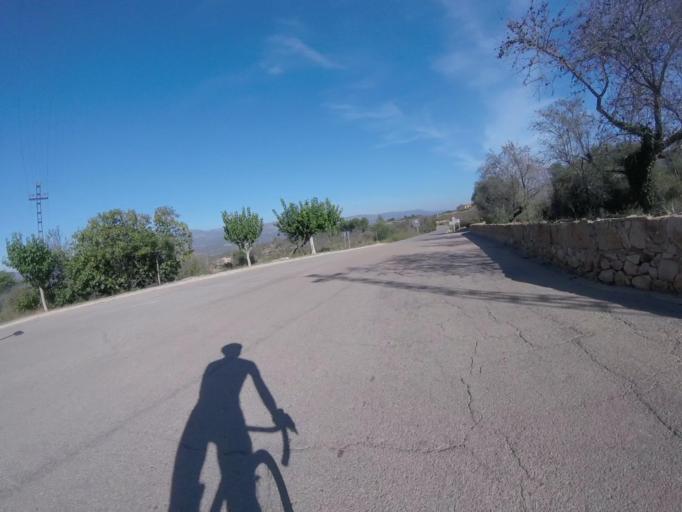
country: ES
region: Valencia
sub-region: Provincia de Castello
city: Benlloch
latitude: 40.2352
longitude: 0.0739
